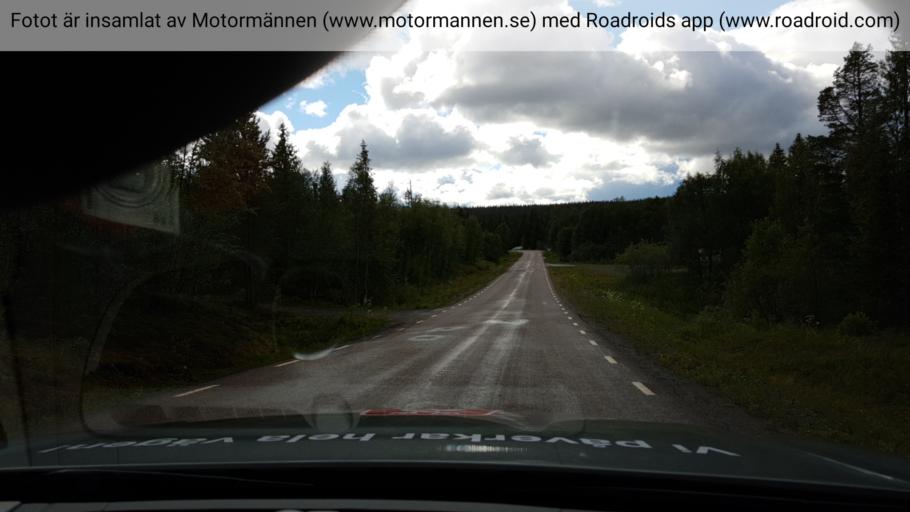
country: SE
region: Jaemtland
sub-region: Are Kommun
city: Jarpen
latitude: 63.0781
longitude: 13.7543
